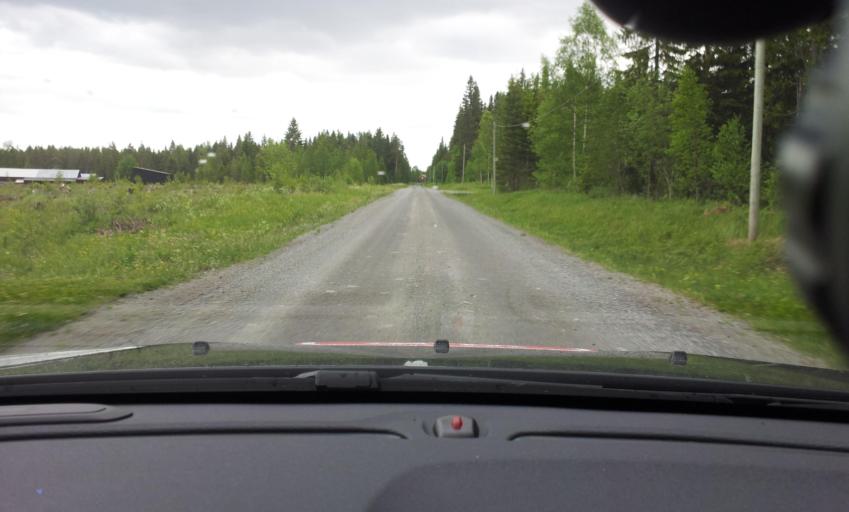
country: SE
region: Jaemtland
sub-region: OEstersunds Kommun
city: Brunflo
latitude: 63.1622
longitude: 15.0045
